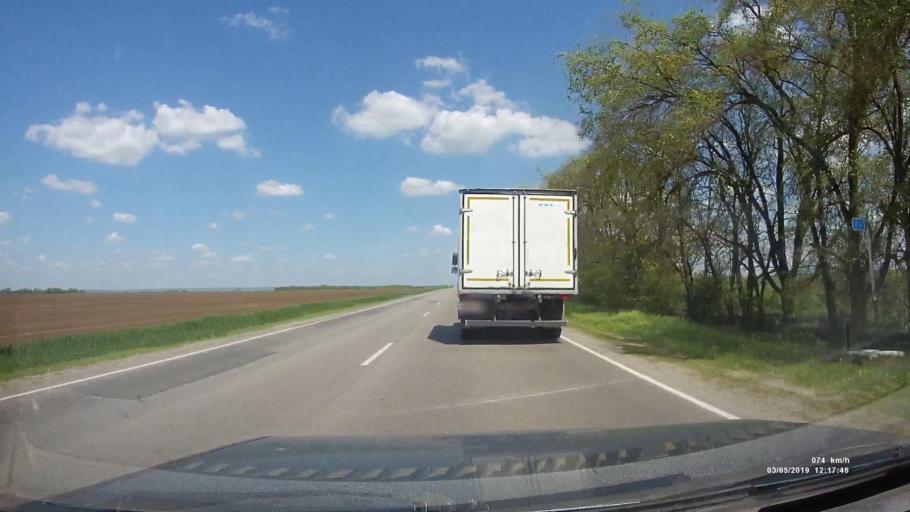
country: RU
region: Rostov
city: Melikhovskaya
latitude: 47.3859
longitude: 40.5947
